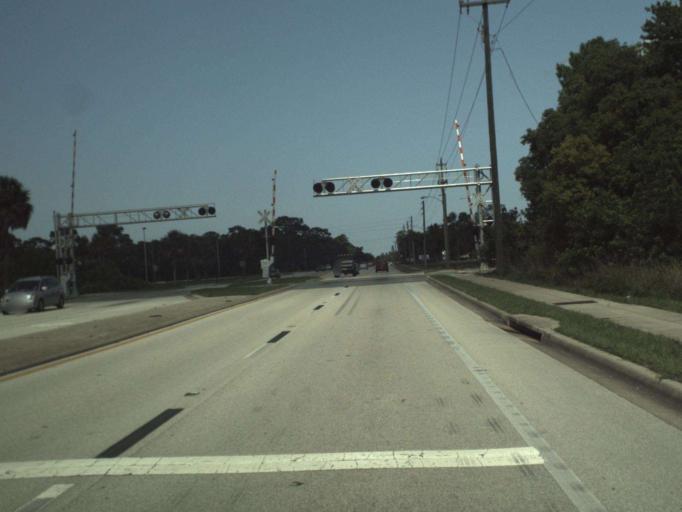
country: US
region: Florida
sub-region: Seminole County
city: Midway
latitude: 28.7603
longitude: -81.2582
